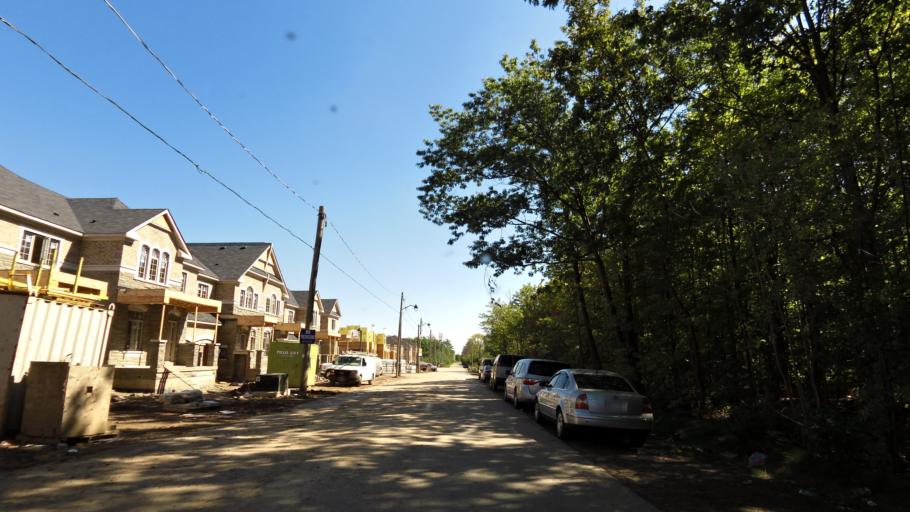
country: CA
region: Ontario
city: Oakville
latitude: 43.4776
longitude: -79.7625
